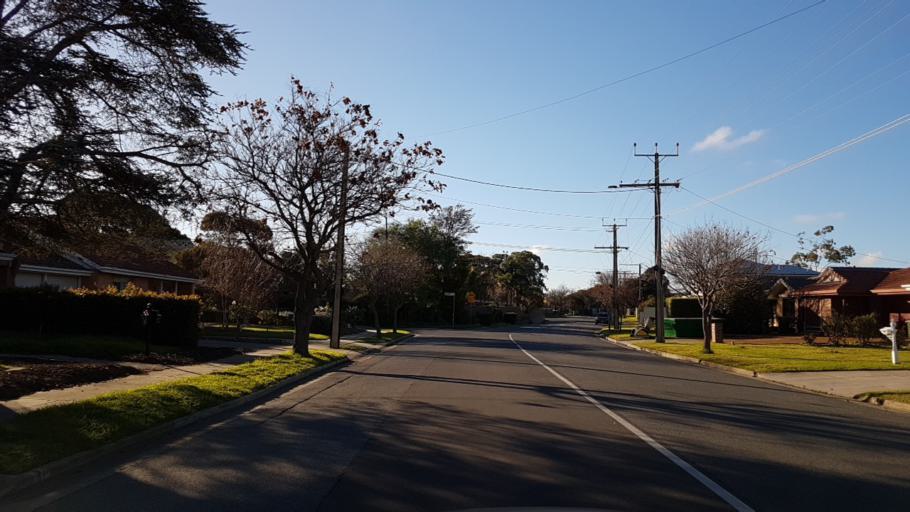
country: AU
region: South Australia
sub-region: City of West Torrens
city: Plympton
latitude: -34.9329
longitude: 138.5241
